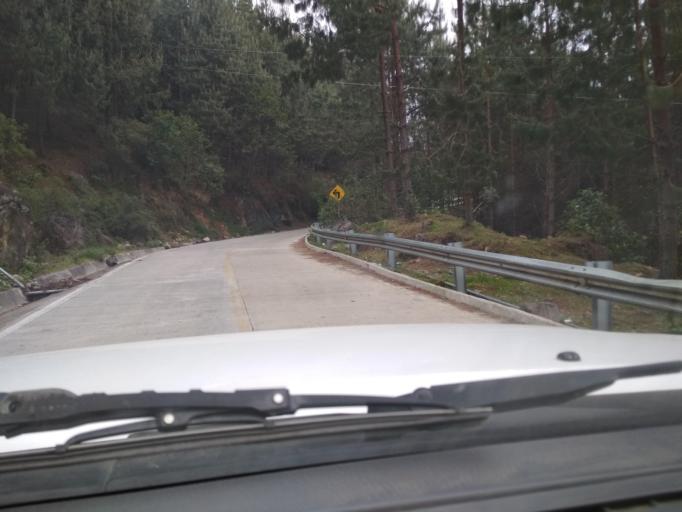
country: MX
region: Veracruz
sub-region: La Perla
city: Chilapa
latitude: 18.9922
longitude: -97.1819
